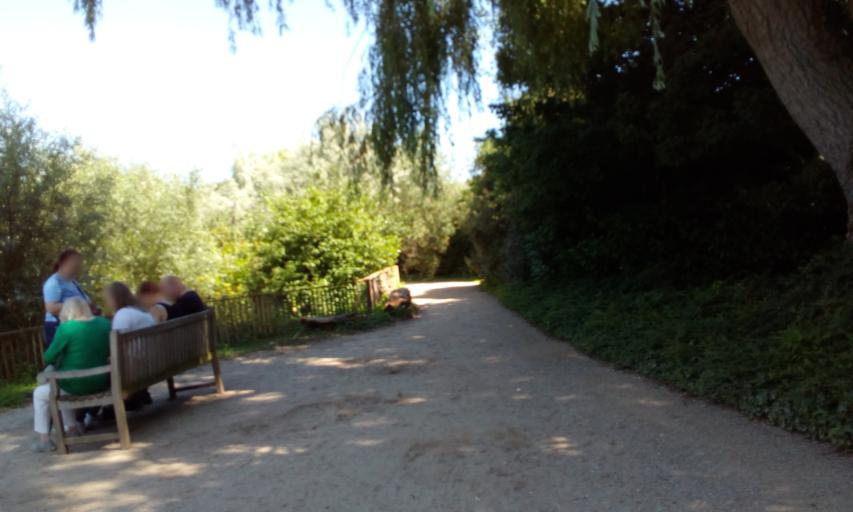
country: NL
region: South Holland
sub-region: Gemeente Alphen aan den Rijn
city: Alphen aan den Rijn
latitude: 52.1378
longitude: 4.6501
